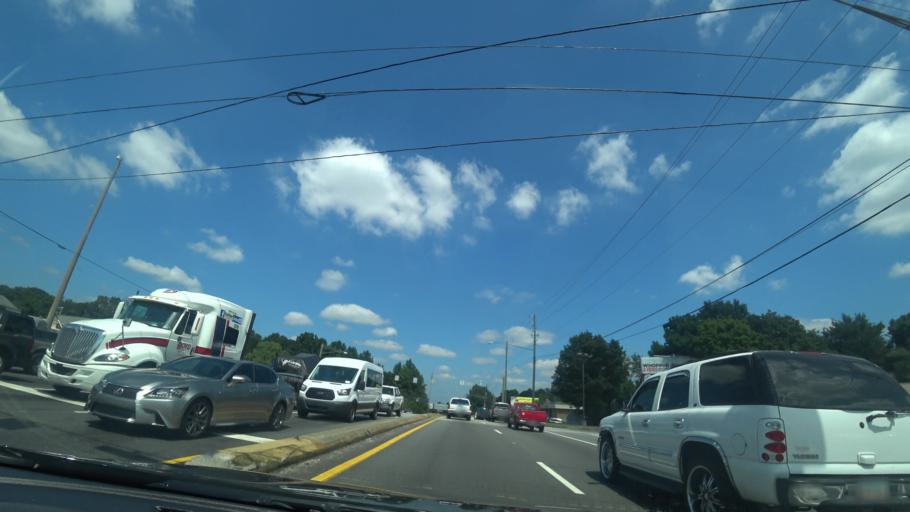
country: US
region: Georgia
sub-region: Gwinnett County
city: Norcross
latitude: 33.9325
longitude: -84.2224
